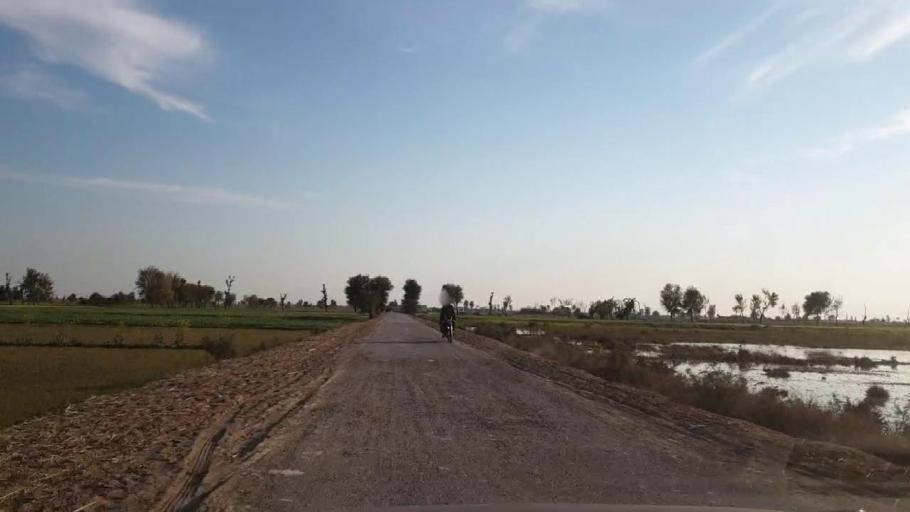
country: PK
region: Sindh
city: Khadro
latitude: 26.1638
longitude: 68.7533
